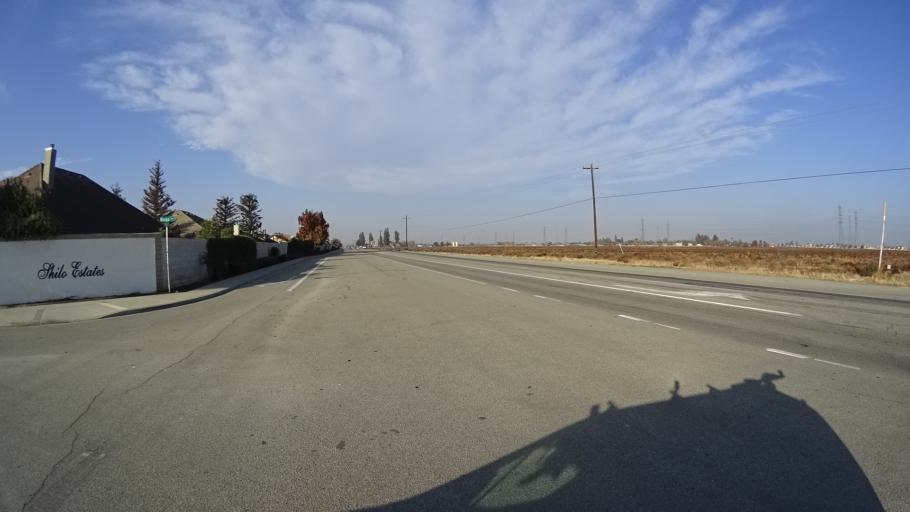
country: US
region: California
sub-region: Kern County
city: Rosedale
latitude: 35.3833
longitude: -119.1722
